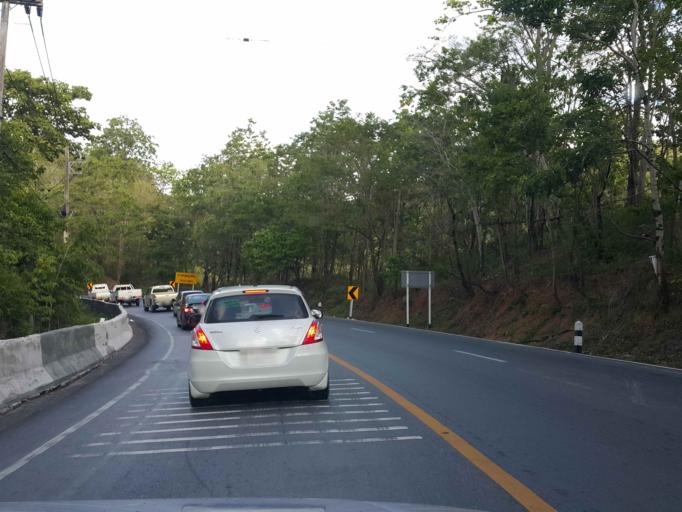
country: TH
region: Tak
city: Tak
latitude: 16.8136
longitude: 98.9718
